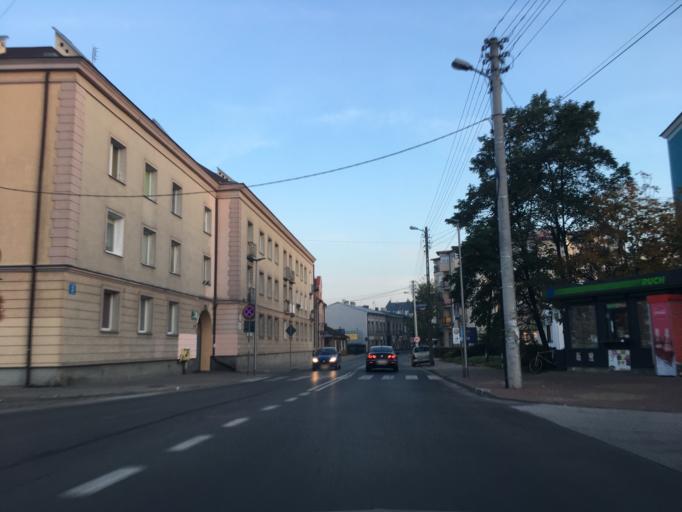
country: PL
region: Lodz Voivodeship
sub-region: Skierniewice
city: Skierniewice
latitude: 51.9574
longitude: 20.1448
